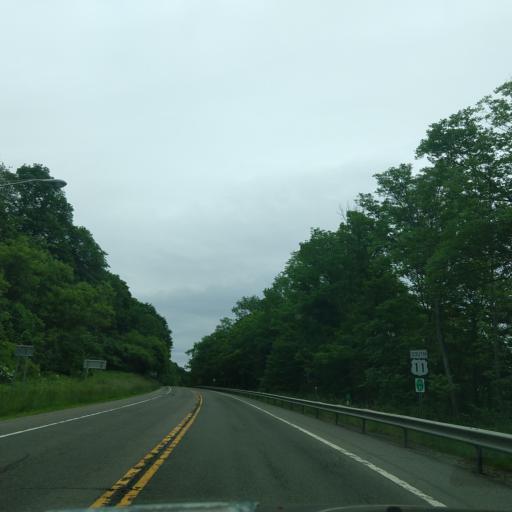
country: US
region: New York
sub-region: Cortland County
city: McGraw
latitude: 42.4917
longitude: -76.0737
